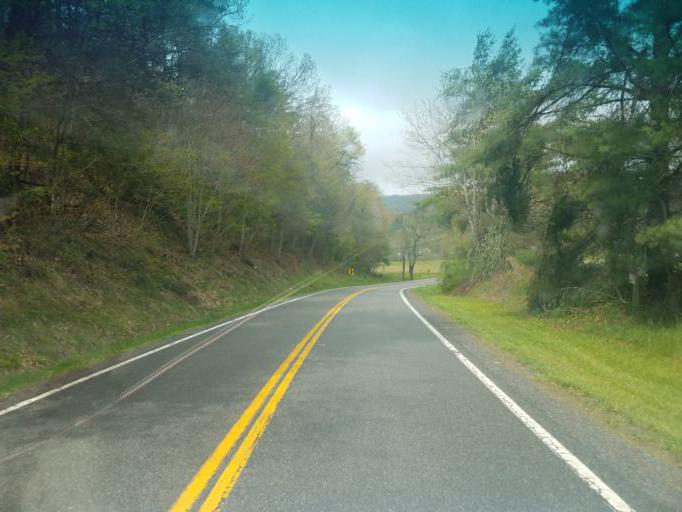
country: US
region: Virginia
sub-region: Bland County
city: Bland
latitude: 37.1726
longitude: -81.1475
